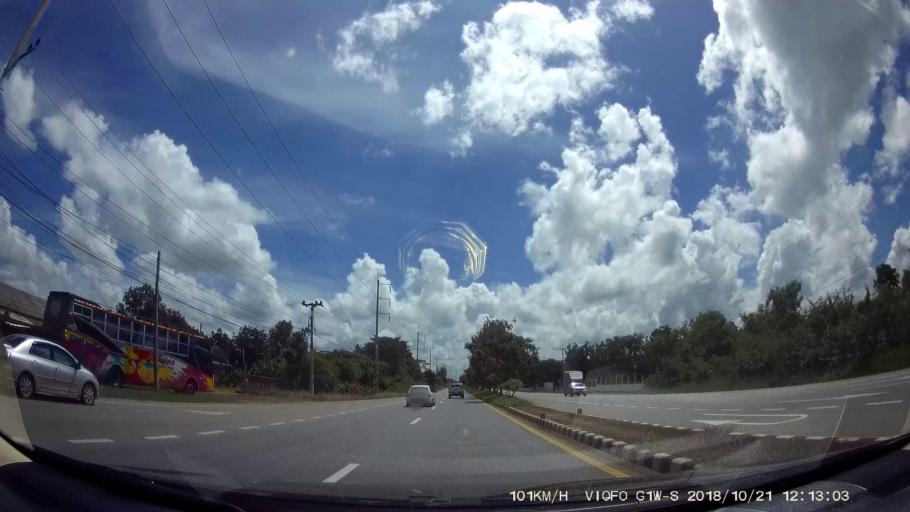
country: TH
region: Chaiyaphum
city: Chatturat
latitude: 15.3989
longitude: 101.8381
